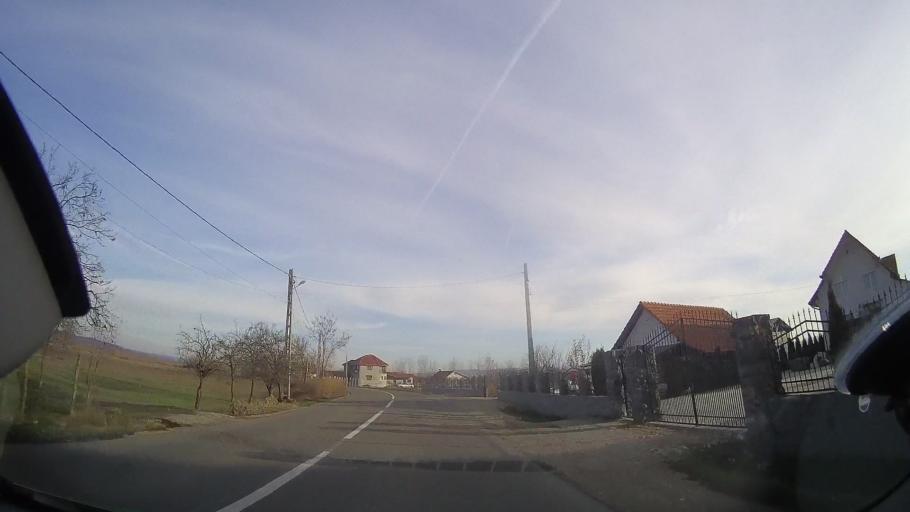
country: RO
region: Bihor
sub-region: Comuna Tileagd
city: Tileagd
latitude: 47.0665
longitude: 22.2122
